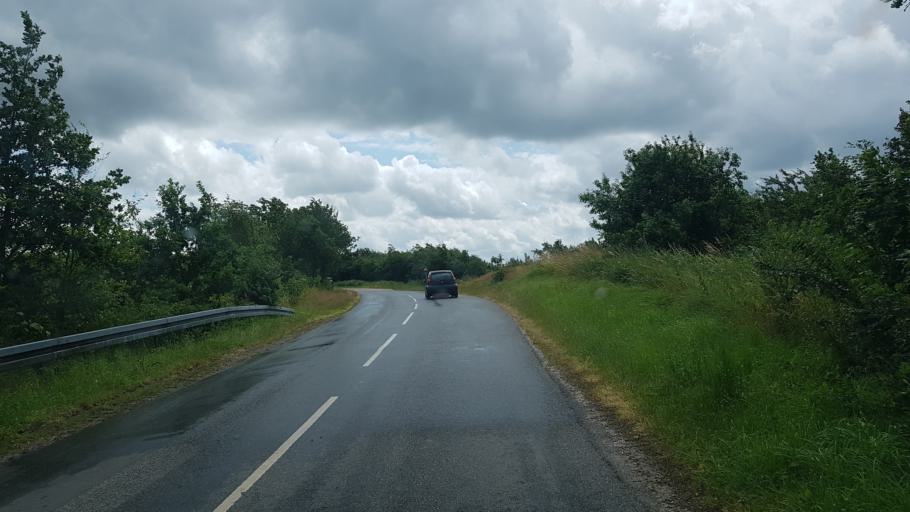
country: DK
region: South Denmark
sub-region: Kolding Kommune
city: Lunderskov
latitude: 55.4716
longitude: 9.2894
